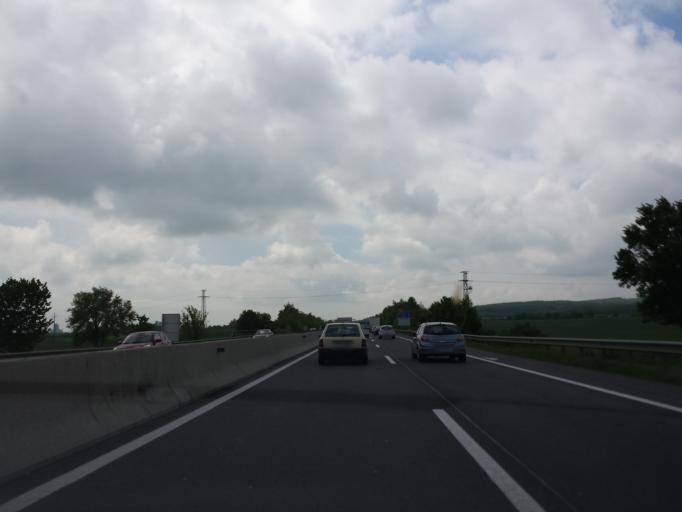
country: AT
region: Burgenland
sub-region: Politischer Bezirk Neusiedl am See
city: Parndorf
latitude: 48.0115
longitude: 16.8359
